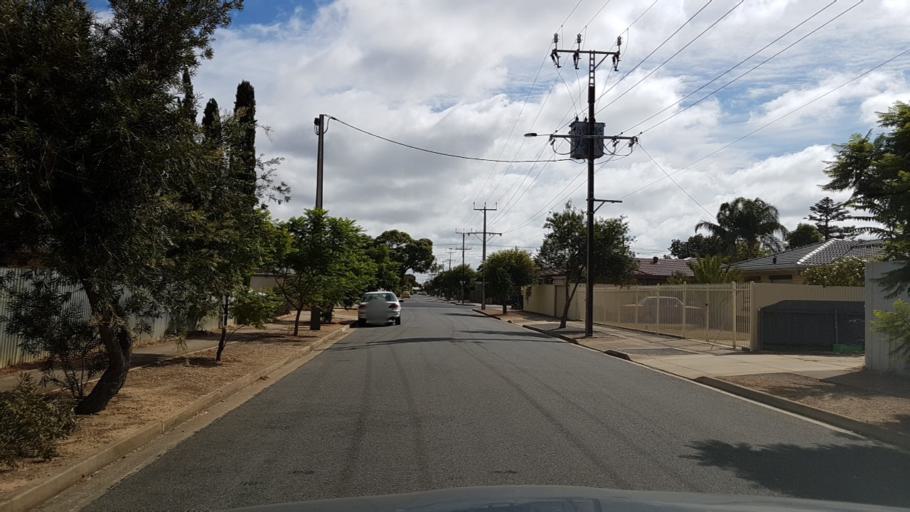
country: AU
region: South Australia
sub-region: Marion
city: Plympton Park
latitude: -34.9872
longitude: 138.5501
